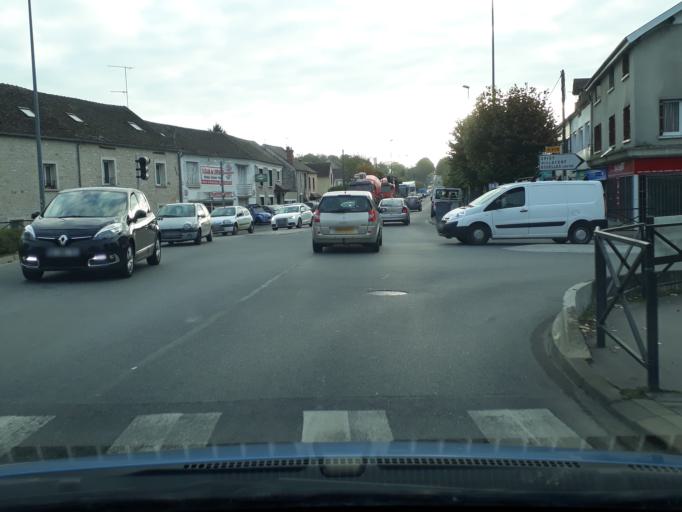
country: FR
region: Ile-de-France
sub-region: Departement de Seine-et-Marne
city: Moret-sur-Loing
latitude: 48.3709
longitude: 2.8262
